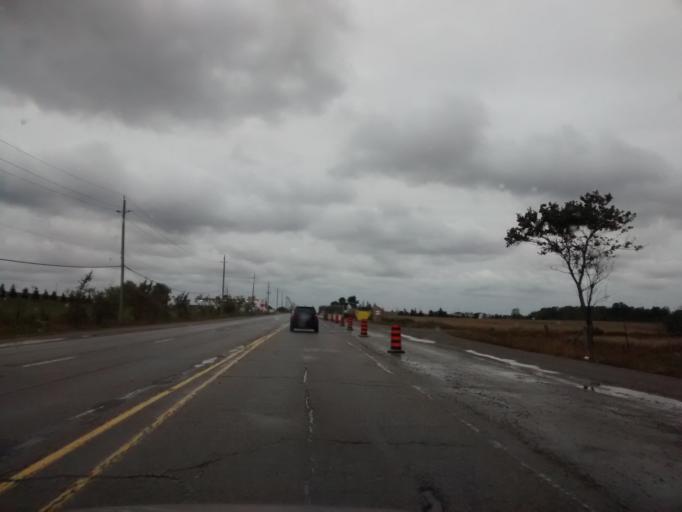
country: CA
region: Ontario
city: Hamilton
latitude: 43.1927
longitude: -79.7682
